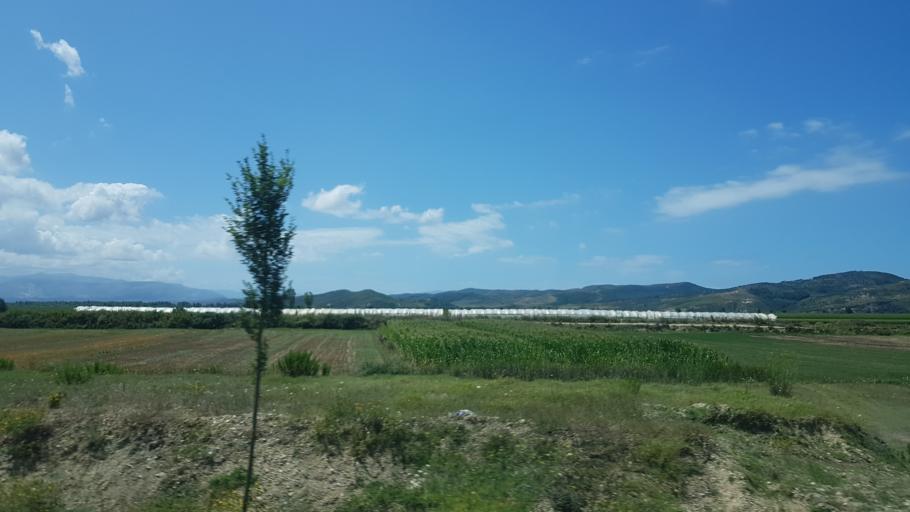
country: AL
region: Fier
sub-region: Rrethi i Fierit
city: Cakran
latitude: 40.5998
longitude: 19.5631
